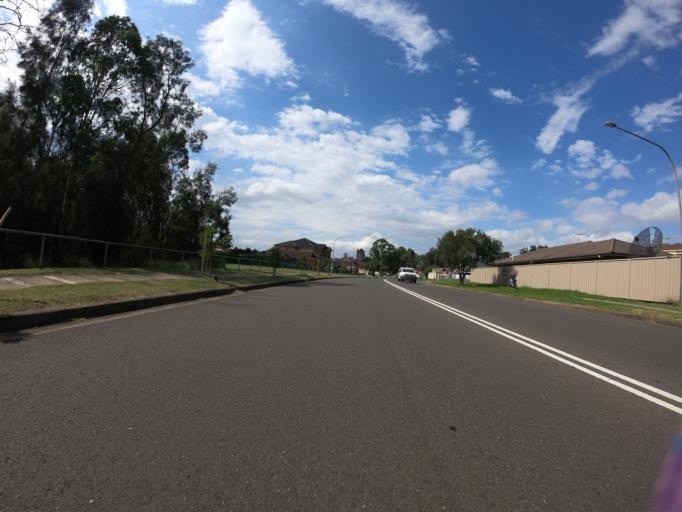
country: AU
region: New South Wales
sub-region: Blacktown
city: Hassall Grove
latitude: -33.7372
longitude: 150.8363
